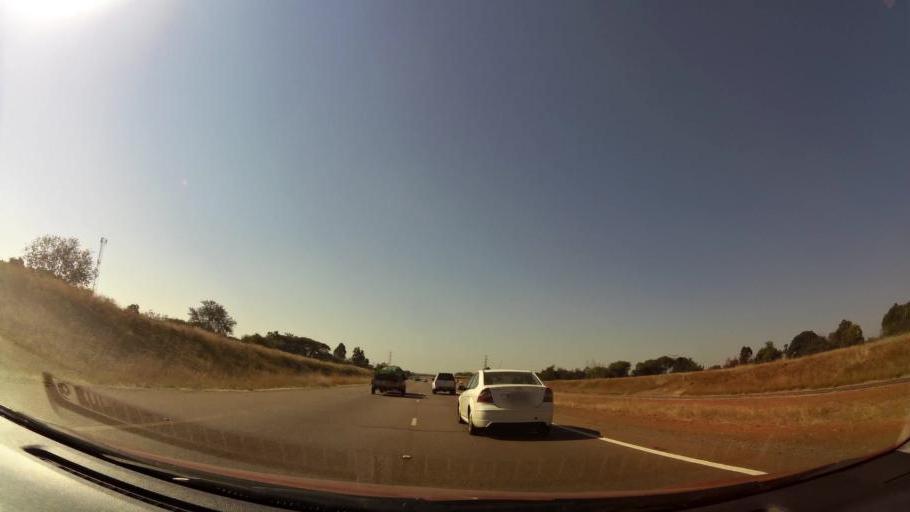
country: ZA
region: North-West
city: Ga-Rankuwa
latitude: -25.6574
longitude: 28.0786
